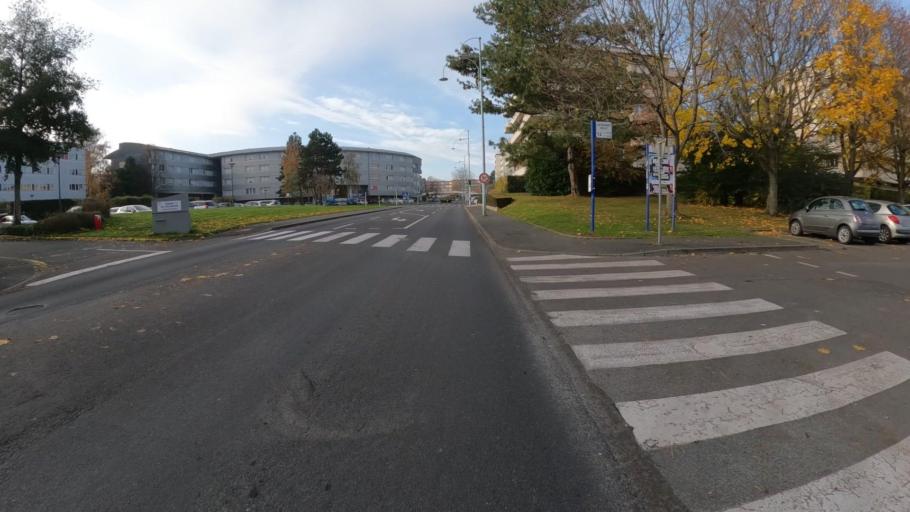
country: FR
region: Lower Normandy
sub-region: Departement du Calvados
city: Caen
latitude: 49.2041
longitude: -0.3357
